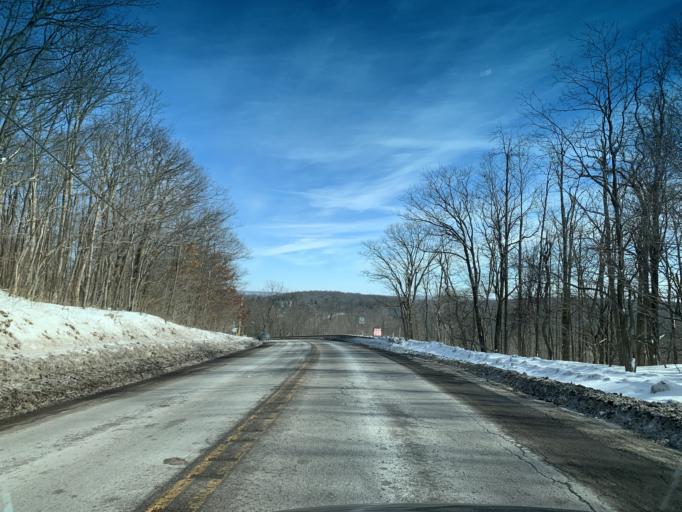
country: US
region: Pennsylvania
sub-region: Somerset County
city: Meyersdale
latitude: 39.6866
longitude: -79.0847
